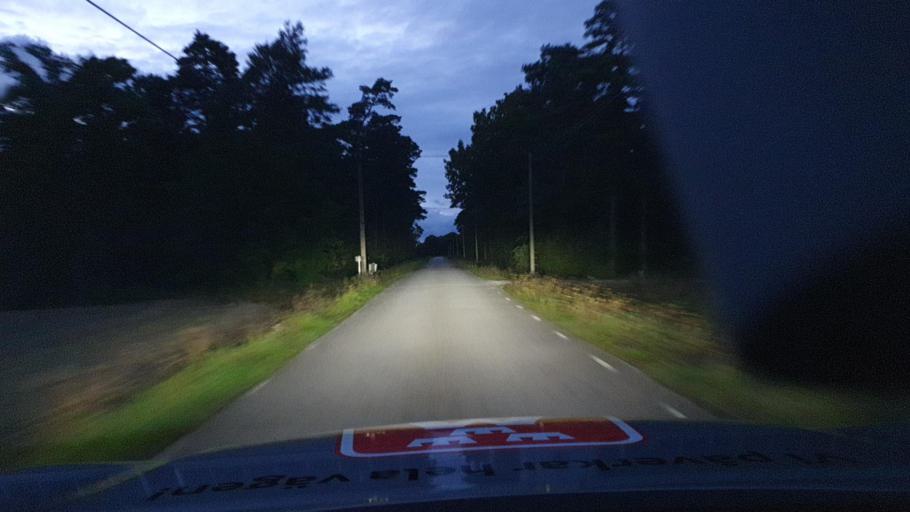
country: SE
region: Gotland
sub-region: Gotland
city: Slite
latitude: 57.7724
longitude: 18.6443
